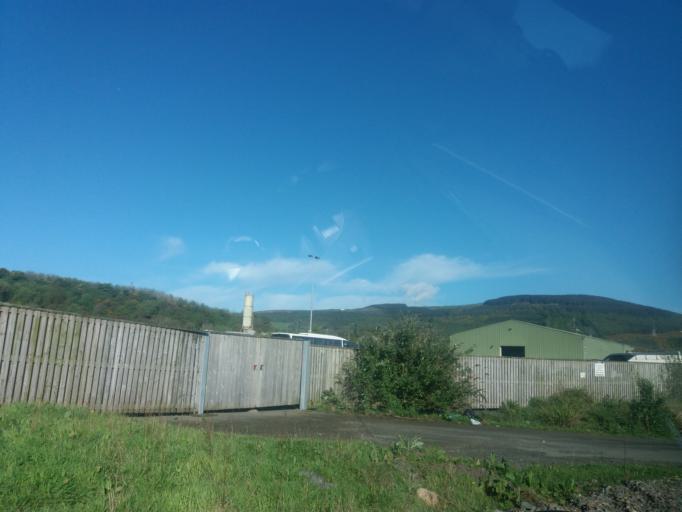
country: IE
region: Leinster
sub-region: Wicklow
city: Kilpedder
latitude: 53.1162
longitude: -6.0985
